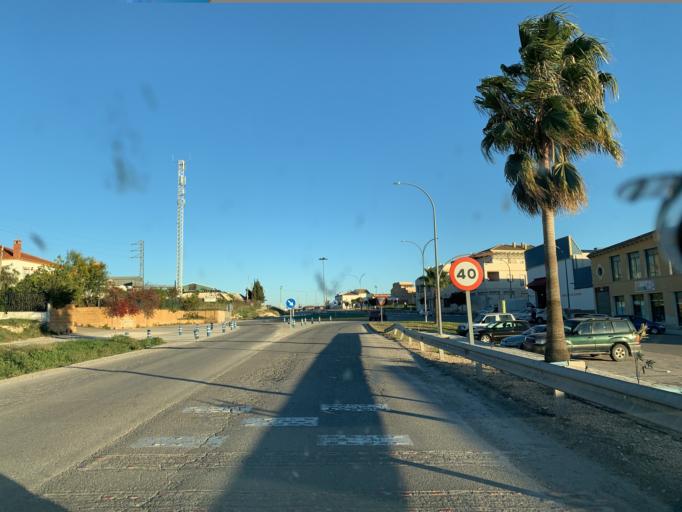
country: ES
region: Andalusia
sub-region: Provincia de Sevilla
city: Pedrera
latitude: 37.2323
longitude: -4.8995
